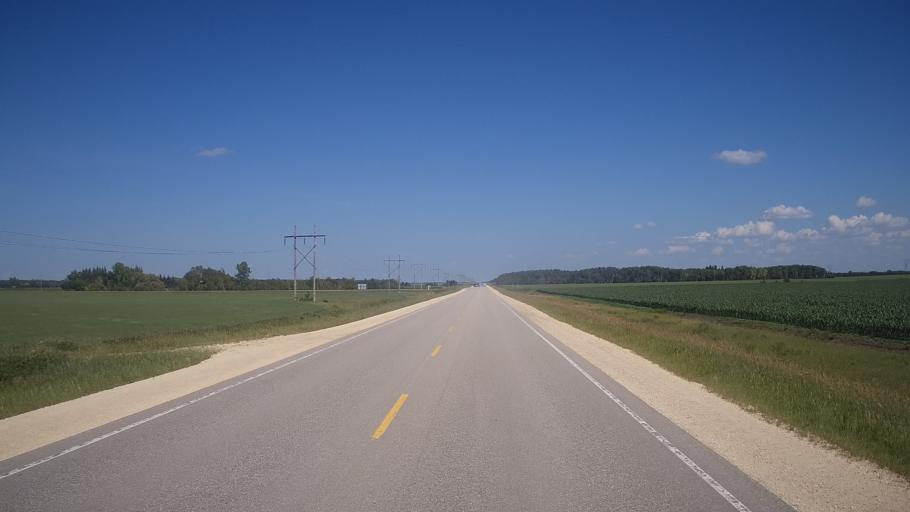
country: CA
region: Manitoba
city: Stonewall
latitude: 50.1227
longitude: -97.4649
